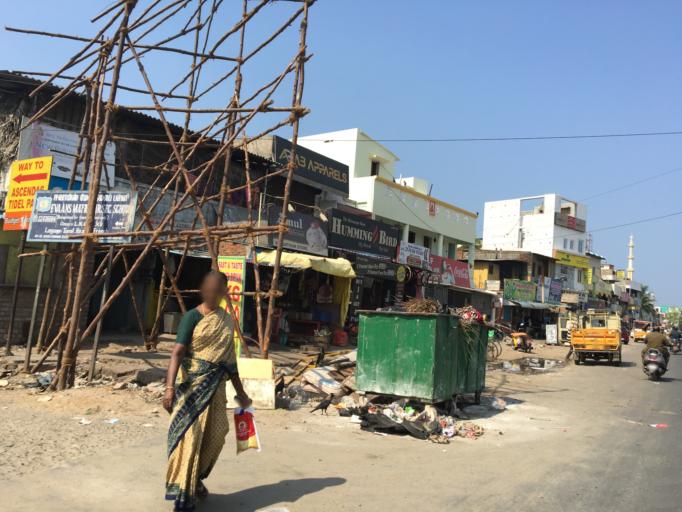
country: IN
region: Tamil Nadu
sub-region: Kancheepuram
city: Perungudi
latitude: 12.9813
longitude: 80.2397
